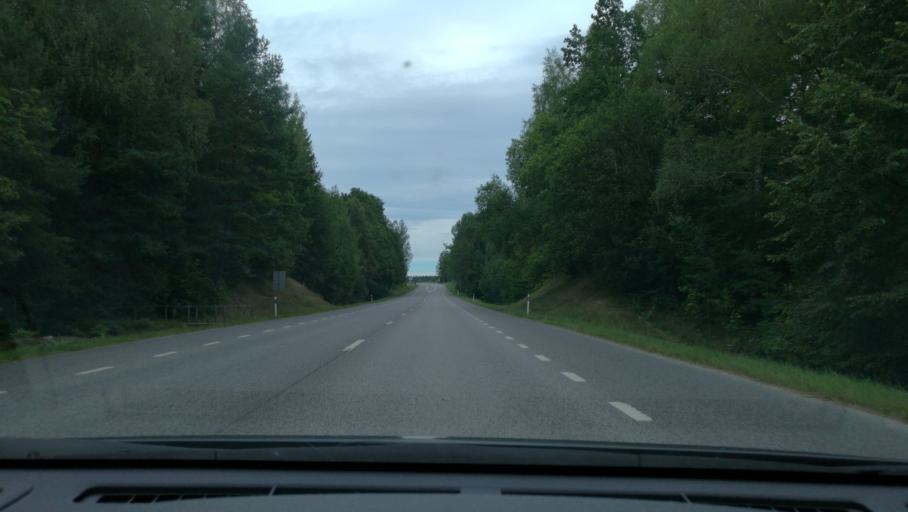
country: SE
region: Soedermanland
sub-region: Katrineholms Kommun
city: Katrineholm
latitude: 58.9732
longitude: 16.2038
